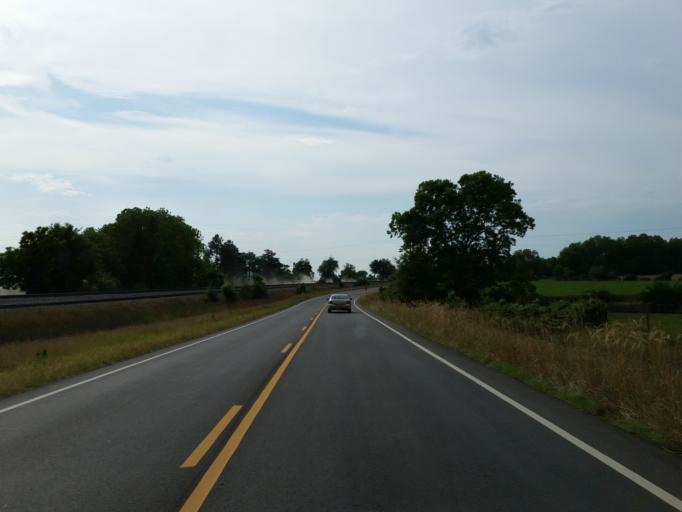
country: US
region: Georgia
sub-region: Turner County
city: Ashburn
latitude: 31.6503
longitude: -83.6264
